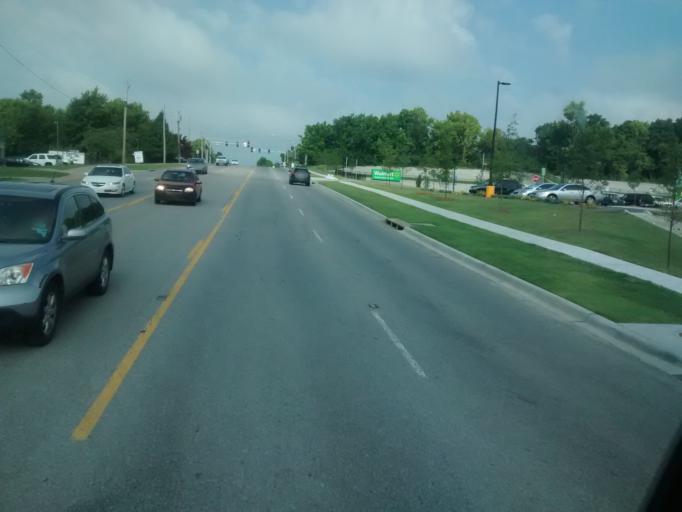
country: US
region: Arkansas
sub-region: Washington County
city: Fayetteville
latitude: 36.0566
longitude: -94.1678
